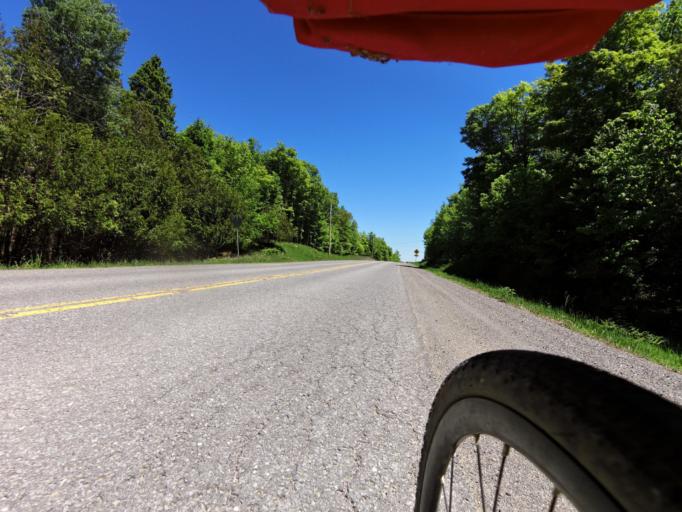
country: CA
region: Ontario
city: Carleton Place
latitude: 45.1841
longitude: -76.3745
